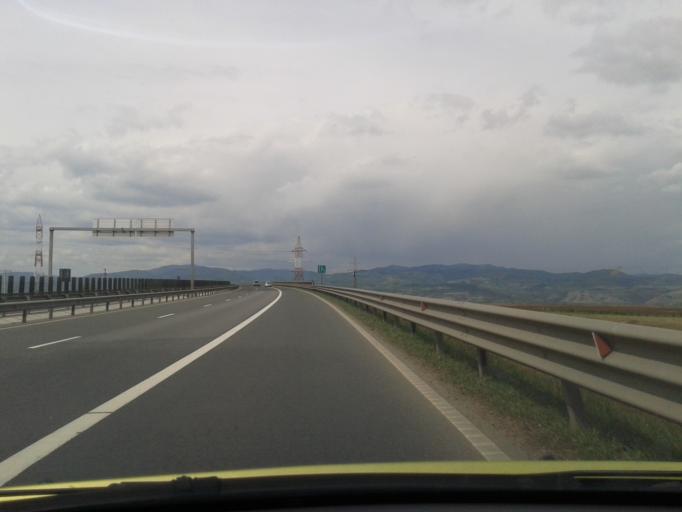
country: RO
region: Alba
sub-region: Municipiul Sebes
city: Lancram
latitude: 45.9775
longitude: 23.5532
